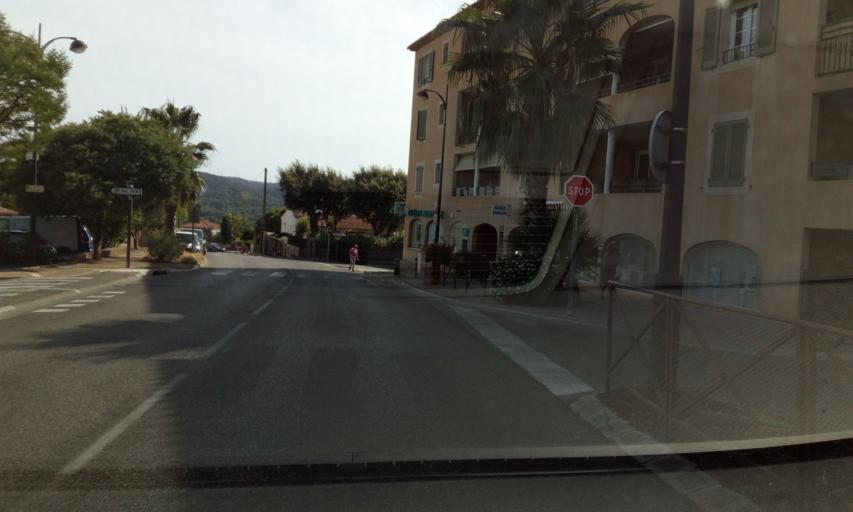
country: FR
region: Provence-Alpes-Cote d'Azur
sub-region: Departement du Var
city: Bormes-les-Mimosas
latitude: 43.1439
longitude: 6.3383
